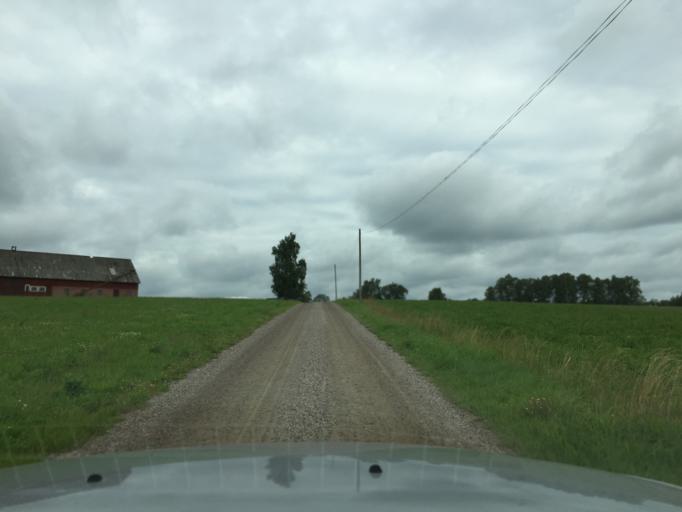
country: SE
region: Skane
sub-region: Hassleholms Kommun
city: Sosdala
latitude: 56.0308
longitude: 13.6581
